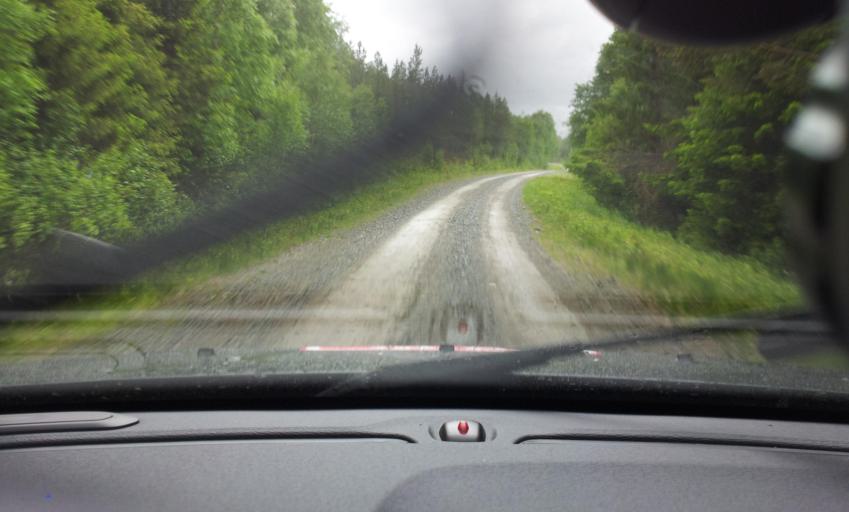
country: SE
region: Jaemtland
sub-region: Are Kommun
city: Are
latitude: 63.1830
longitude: 13.1424
